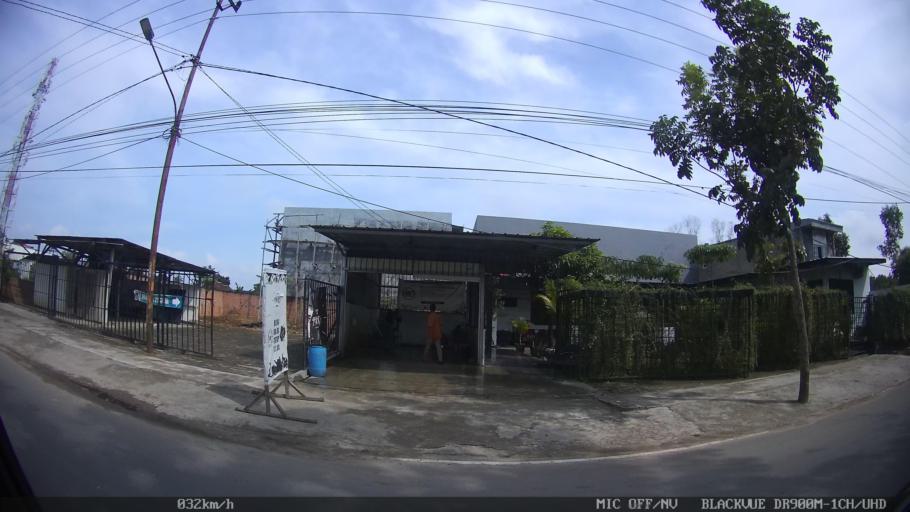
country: ID
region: Lampung
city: Kedaton
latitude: -5.3810
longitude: 105.2999
